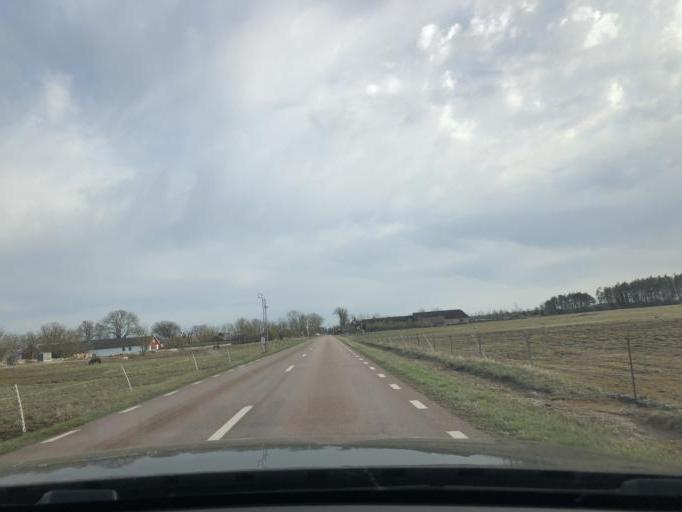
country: SE
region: Kalmar
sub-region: Morbylanga Kommun
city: Sodra Sandby
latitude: 56.5701
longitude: 16.6182
